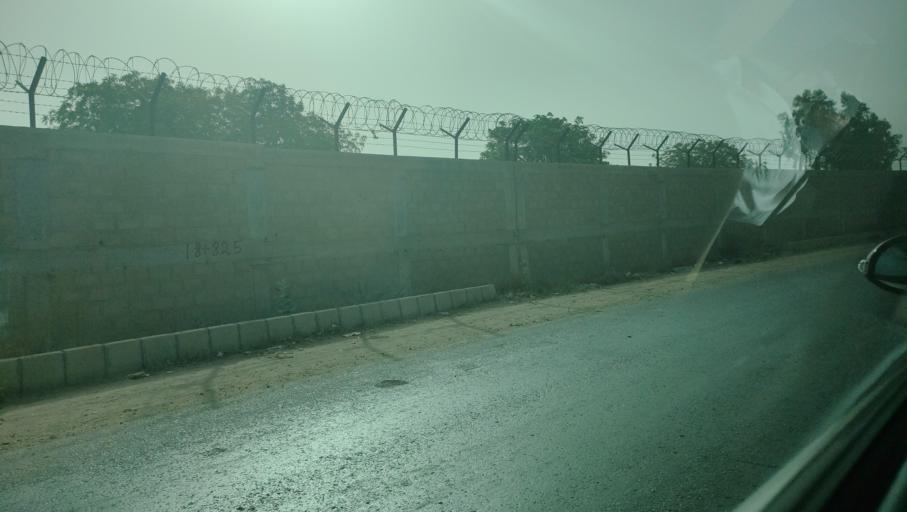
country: PK
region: Sindh
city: Malir Cantonment
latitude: 24.9153
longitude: 67.1887
